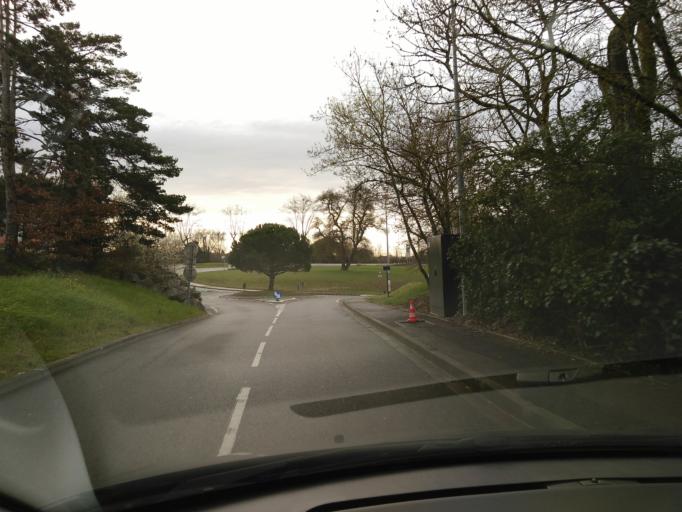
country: FR
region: Midi-Pyrenees
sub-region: Departement de la Haute-Garonne
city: Rouffiac-Tolosan
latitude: 43.6703
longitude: 1.5145
